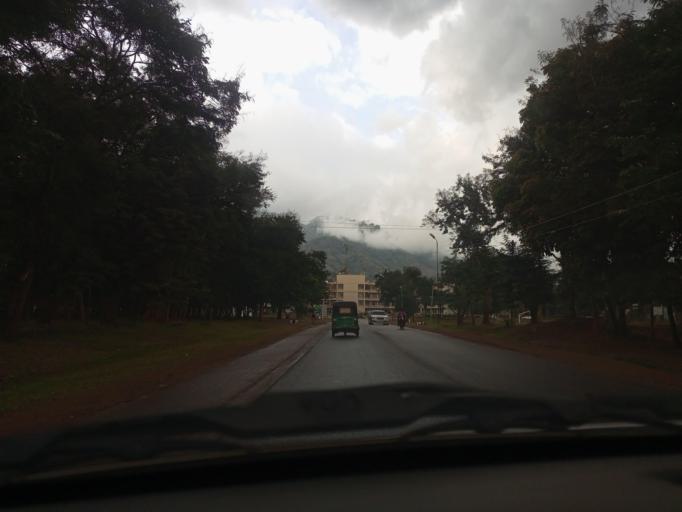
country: TZ
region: Morogoro
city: Morogoro
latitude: -6.8501
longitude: 37.6577
